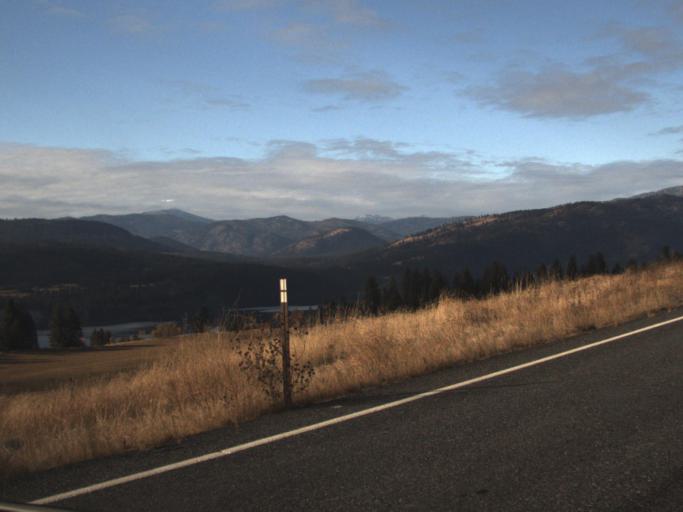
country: US
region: Washington
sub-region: Stevens County
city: Kettle Falls
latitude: 48.4059
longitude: -118.1705
